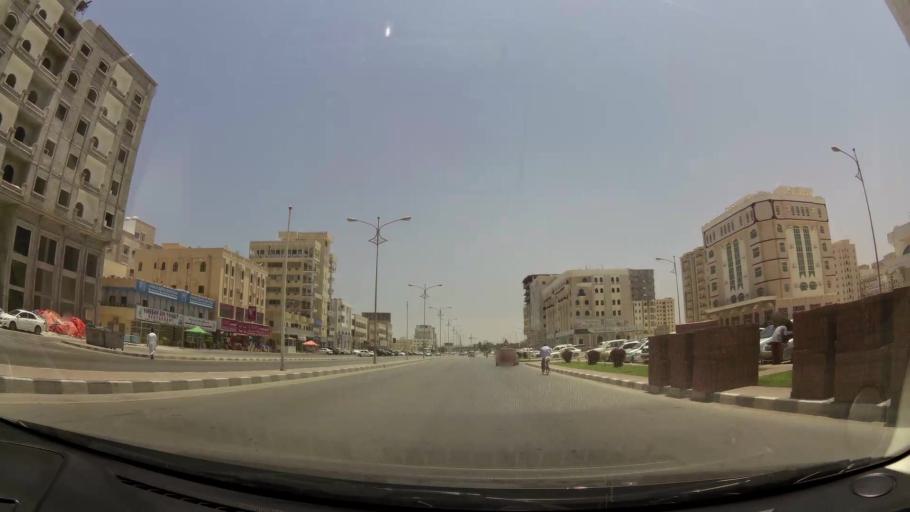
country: OM
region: Zufar
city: Salalah
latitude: 17.0171
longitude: 54.0986
